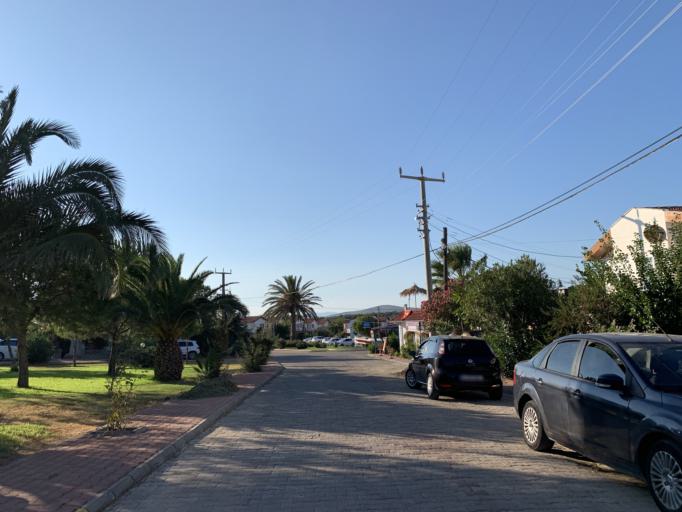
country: TR
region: Balikesir
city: Ayvalik
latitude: 39.3510
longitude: 26.6501
